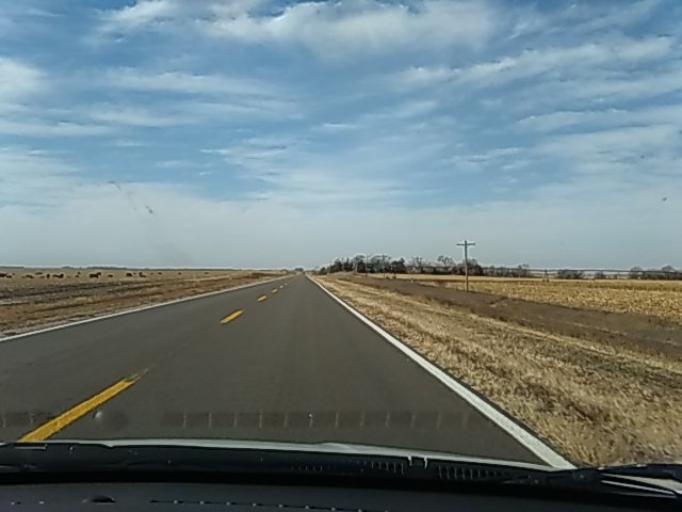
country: US
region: Nebraska
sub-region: Clay County
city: Clay Center
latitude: 40.4232
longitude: -97.9596
